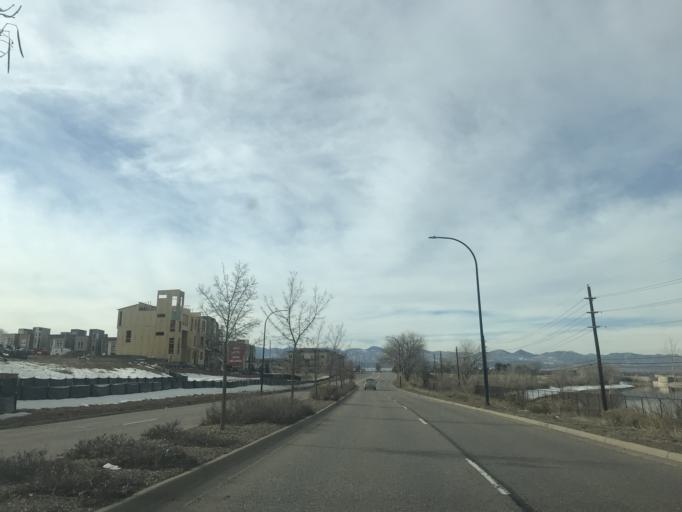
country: US
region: Colorado
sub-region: Arapahoe County
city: Columbine Valley
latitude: 39.5663
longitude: -105.0181
